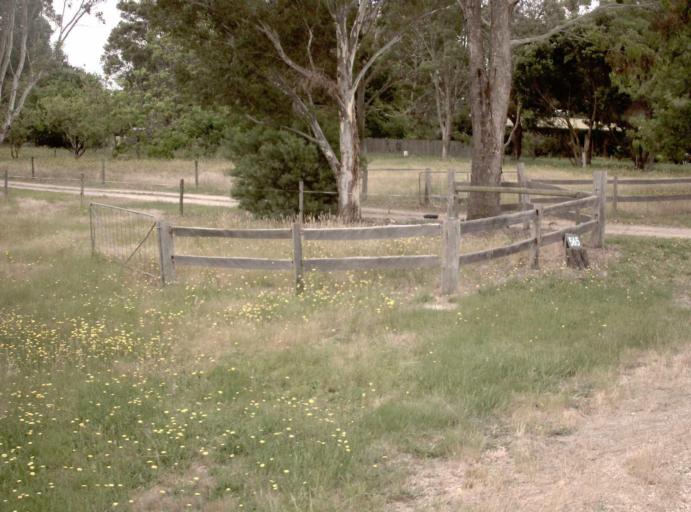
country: AU
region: Victoria
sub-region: East Gippsland
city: Bairnsdale
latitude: -37.8309
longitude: 147.4334
